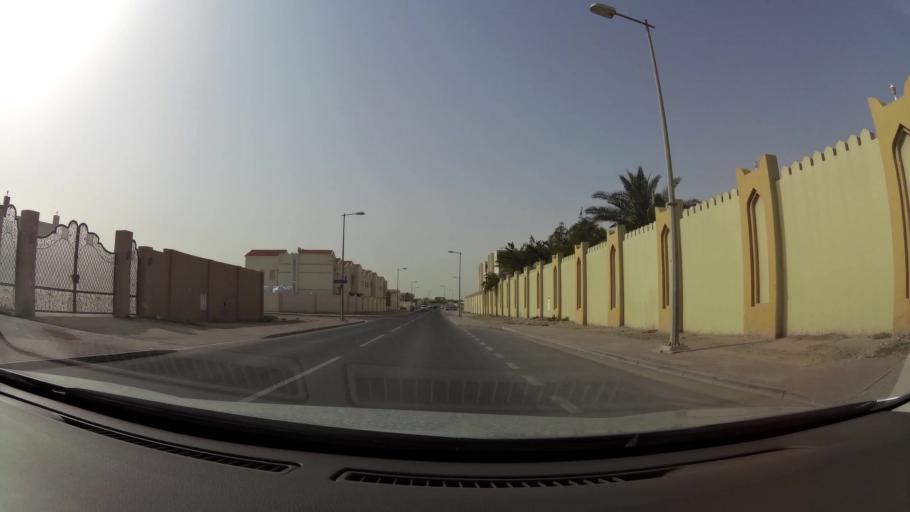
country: QA
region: Baladiyat ar Rayyan
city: Ar Rayyan
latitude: 25.2403
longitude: 51.4403
